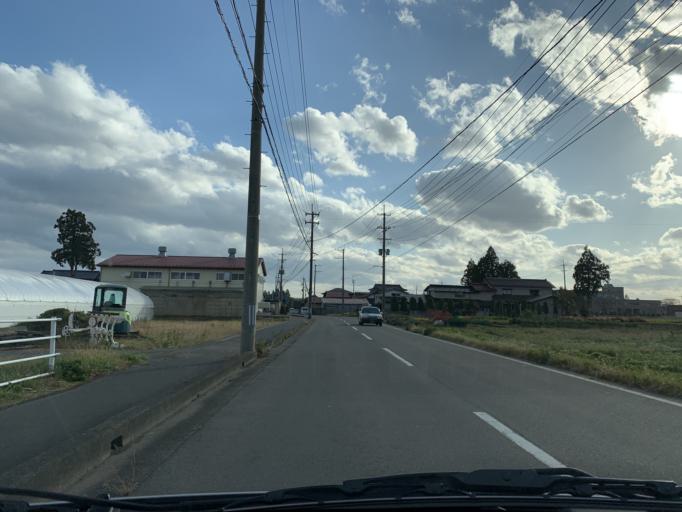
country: JP
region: Iwate
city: Mizusawa
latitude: 39.1459
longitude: 141.1589
